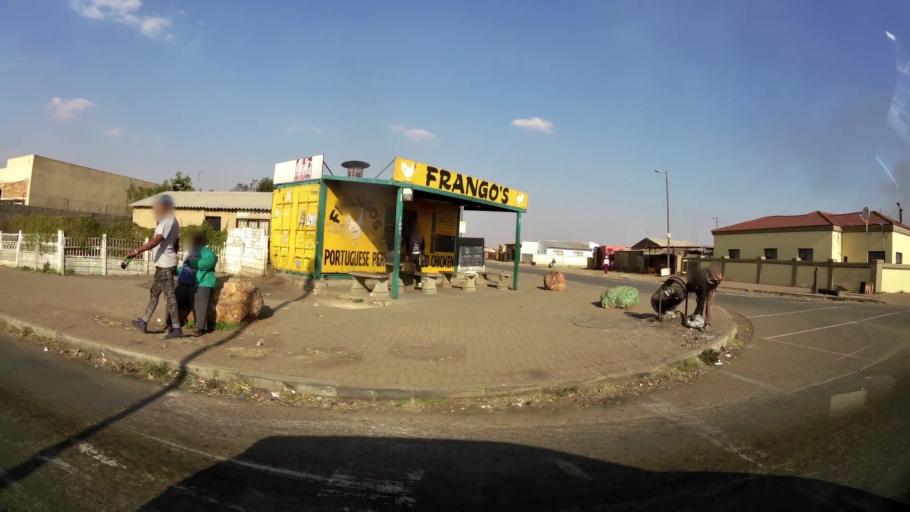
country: ZA
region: Gauteng
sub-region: Ekurhuleni Metropolitan Municipality
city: Brakpan
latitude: -26.1463
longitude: 28.4203
